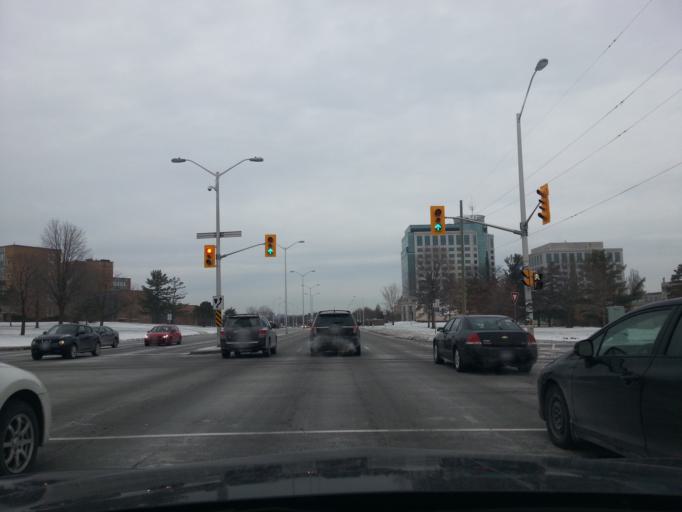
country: CA
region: Ontario
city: Ottawa
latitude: 45.3730
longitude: -75.6908
